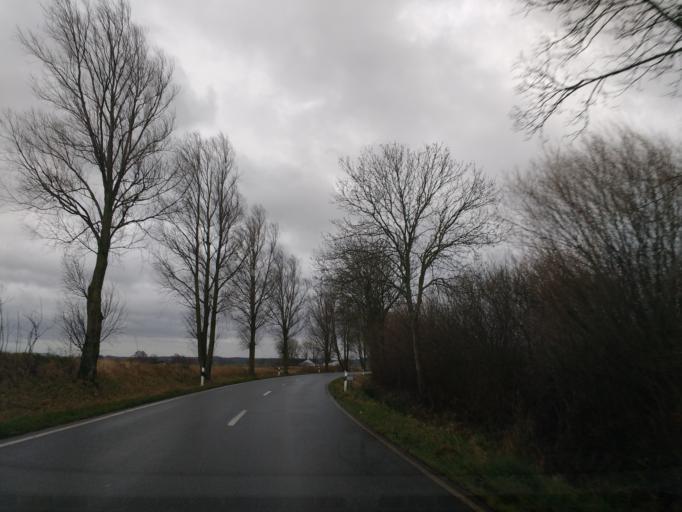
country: DE
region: Schleswig-Holstein
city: Blekendorf
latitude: 54.3130
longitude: 10.6572
